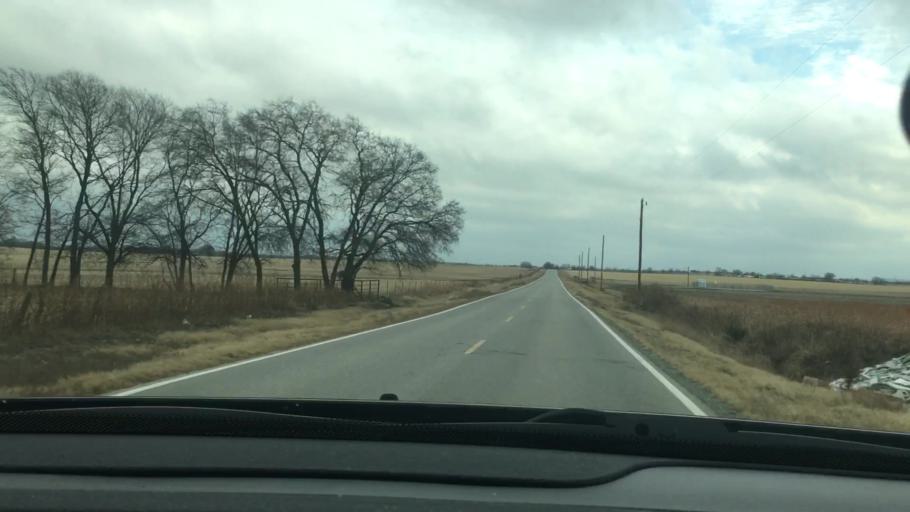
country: US
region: Oklahoma
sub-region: Bryan County
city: Durant
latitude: 34.0887
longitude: -96.4708
